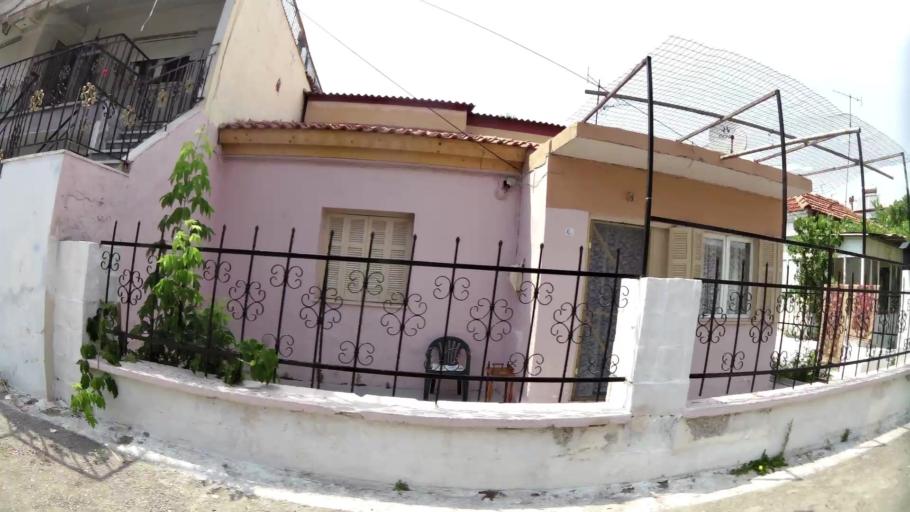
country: GR
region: Central Macedonia
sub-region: Nomos Thessalonikis
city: Menemeni
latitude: 40.6574
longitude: 22.8998
